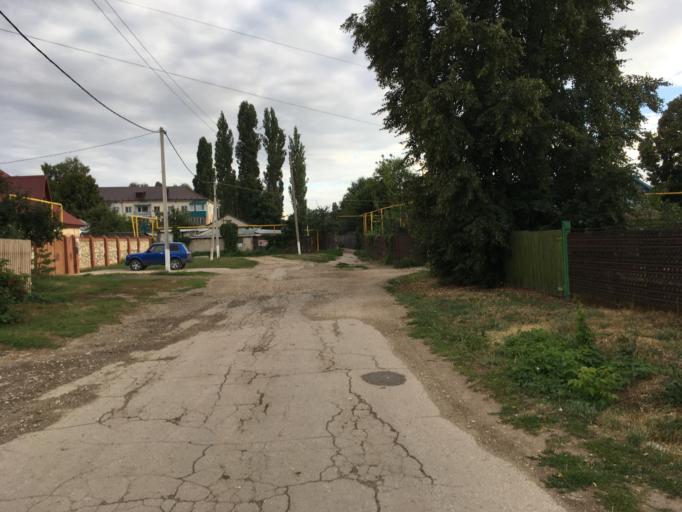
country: RU
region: Samara
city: Bezenchuk
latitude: 52.9857
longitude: 49.4441
